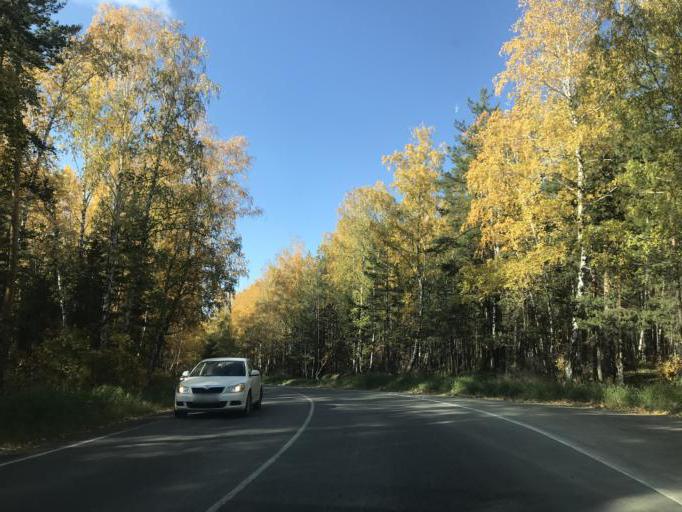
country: RU
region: Chelyabinsk
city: Dolgoderevenskoye
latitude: 55.2823
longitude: 61.3631
